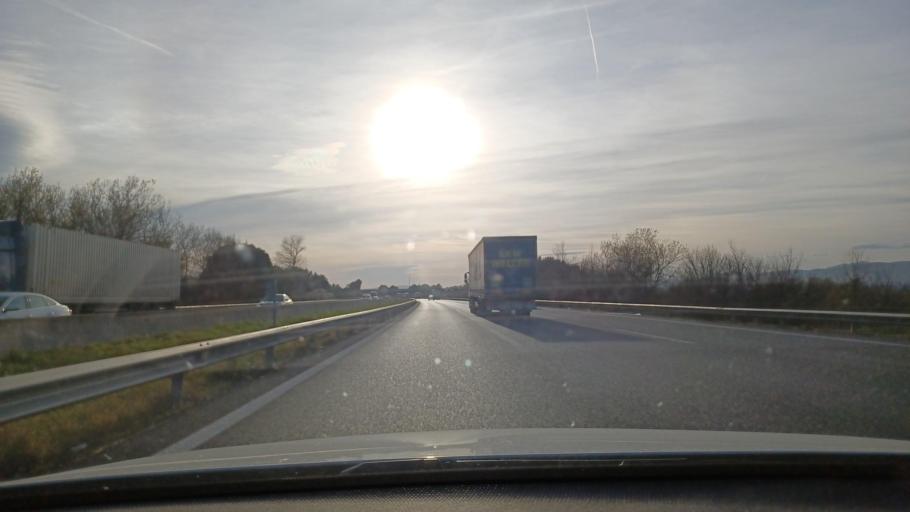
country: ES
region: Catalonia
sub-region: Provincia de Barcelona
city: Vilafranca del Penedes
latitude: 41.3277
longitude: 1.6510
